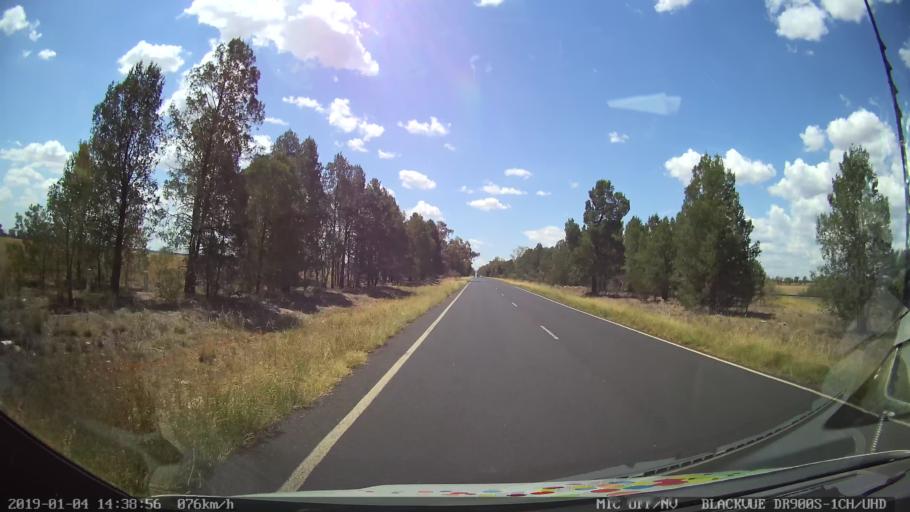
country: AU
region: New South Wales
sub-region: Dubbo Municipality
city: Dubbo
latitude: -32.1706
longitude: 148.6320
